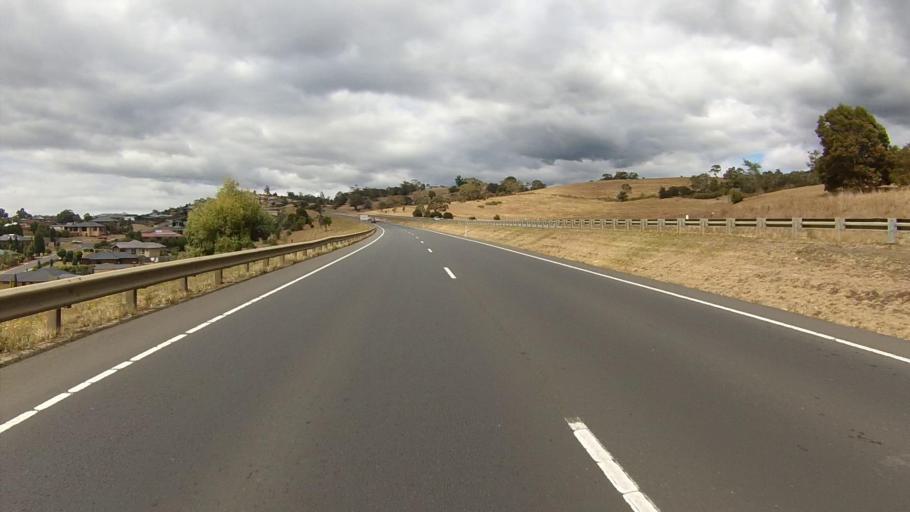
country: AU
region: Tasmania
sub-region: Glenorchy
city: Austins Ferry
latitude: -42.7656
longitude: 147.2355
